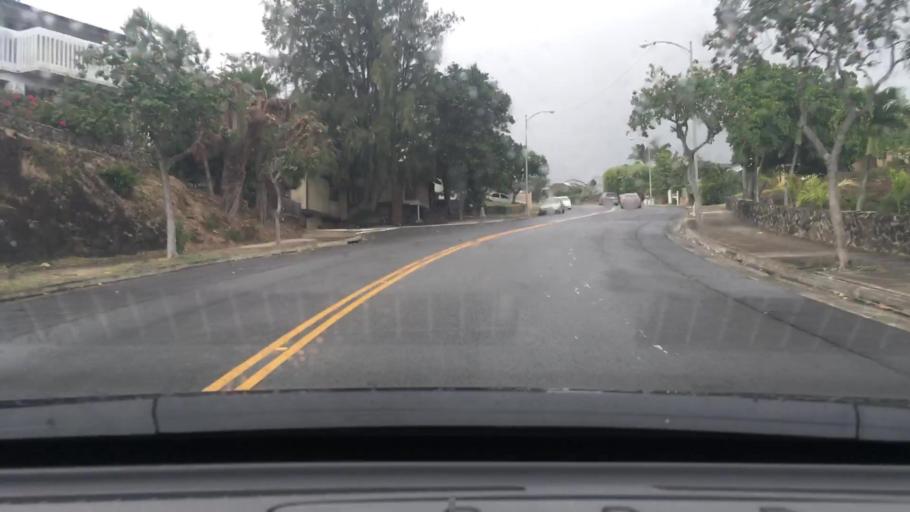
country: US
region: Hawaii
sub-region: Honolulu County
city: Waimanalo Beach
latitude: 21.2925
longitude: -157.7026
